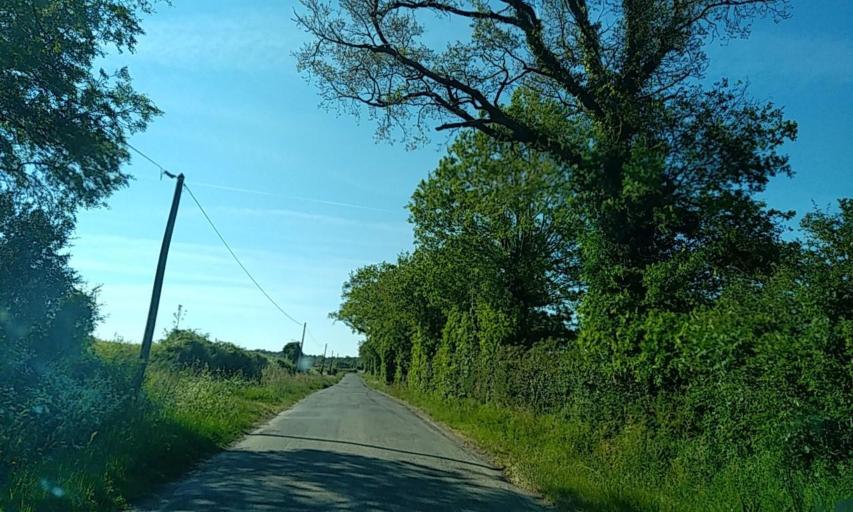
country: FR
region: Poitou-Charentes
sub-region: Departement des Deux-Sevres
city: Boisme
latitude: 46.7947
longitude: -0.4318
